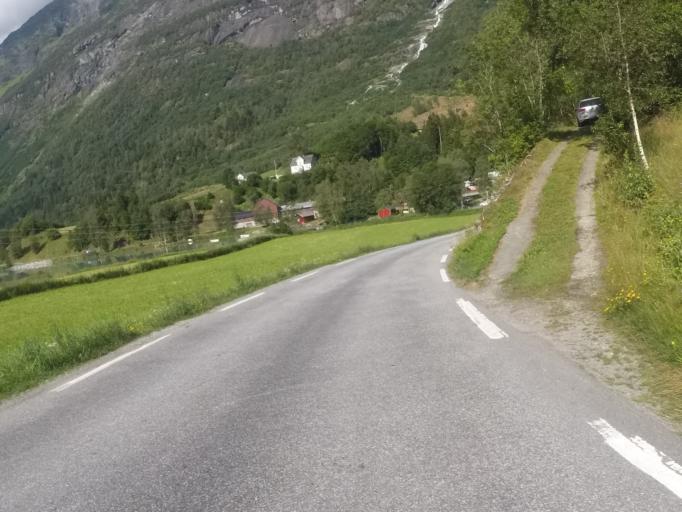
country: NO
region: Sogn og Fjordane
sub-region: Stryn
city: Stryn
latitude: 61.7573
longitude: 6.8151
